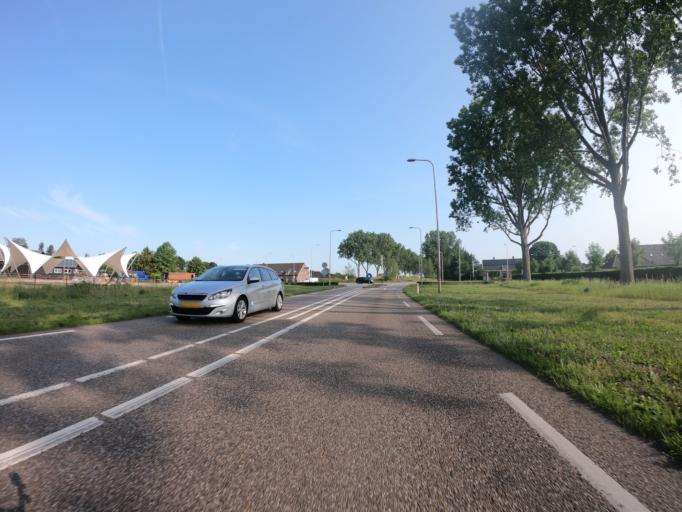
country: NL
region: North Brabant
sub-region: Gemeente Landerd
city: Reek
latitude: 51.7429
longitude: 5.6676
